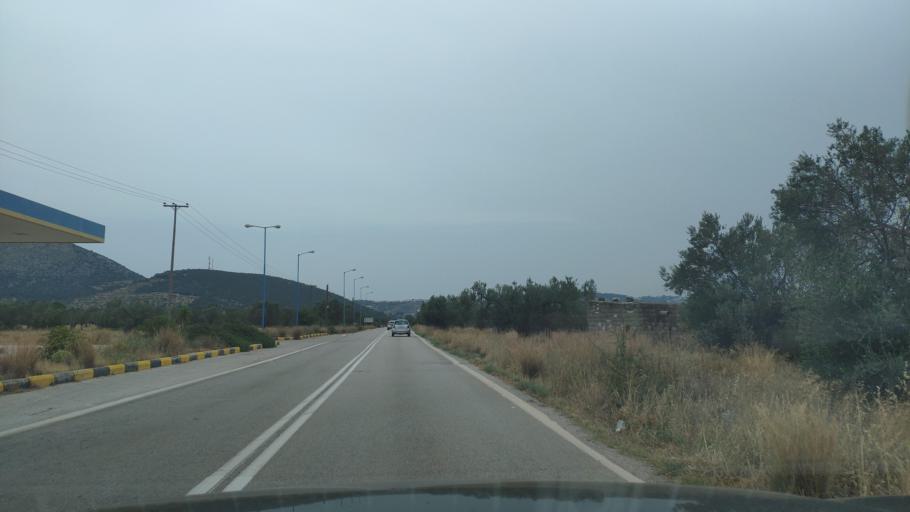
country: GR
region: Peloponnese
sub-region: Nomos Argolidos
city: Koilas
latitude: 37.4112
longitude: 23.1530
